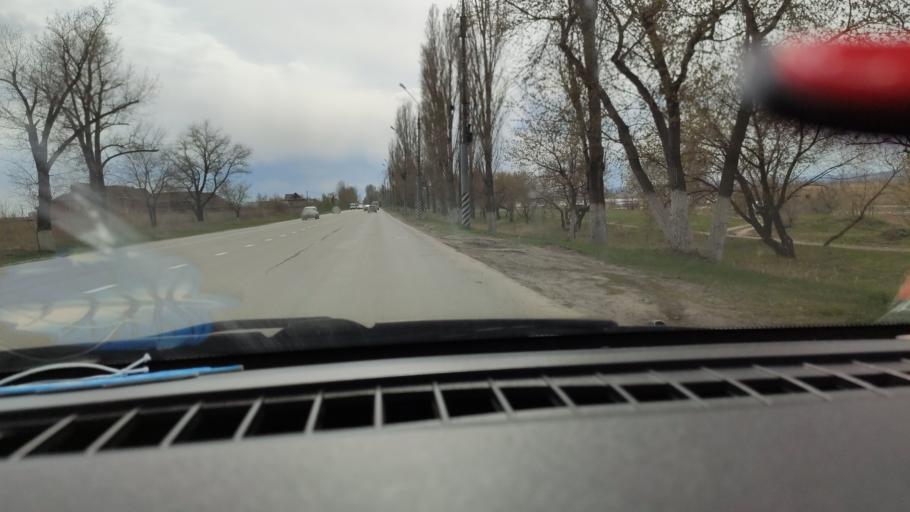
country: RU
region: Saratov
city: Privolzhskiy
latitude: 51.4349
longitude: 46.0596
